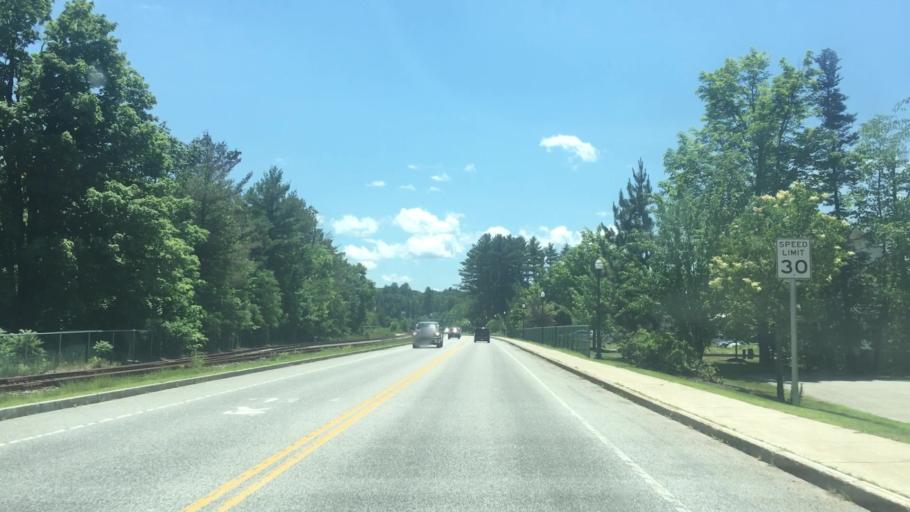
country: US
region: New Hampshire
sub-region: Carroll County
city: North Conway
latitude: 44.0505
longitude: -71.1237
